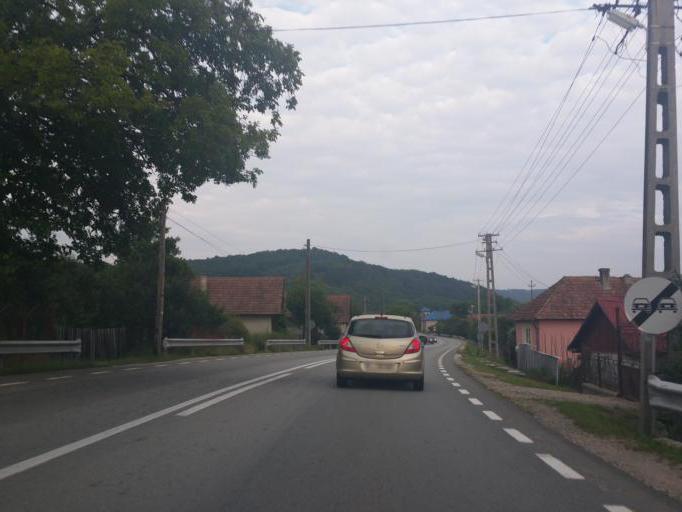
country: RO
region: Salaj
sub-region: Comuna Sanmihaiu Almasului
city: Sanmihaiu Almasului
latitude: 46.9574
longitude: 23.3418
